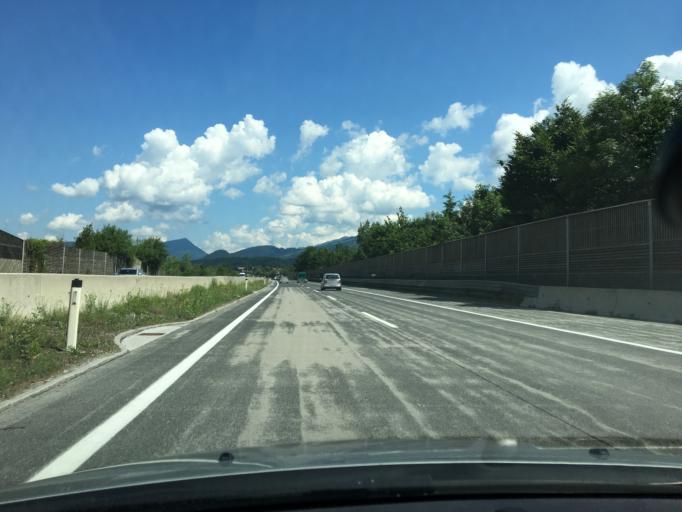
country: AT
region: Salzburg
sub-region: Politischer Bezirk Hallein
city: Kuchl
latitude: 47.6361
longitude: 13.1339
